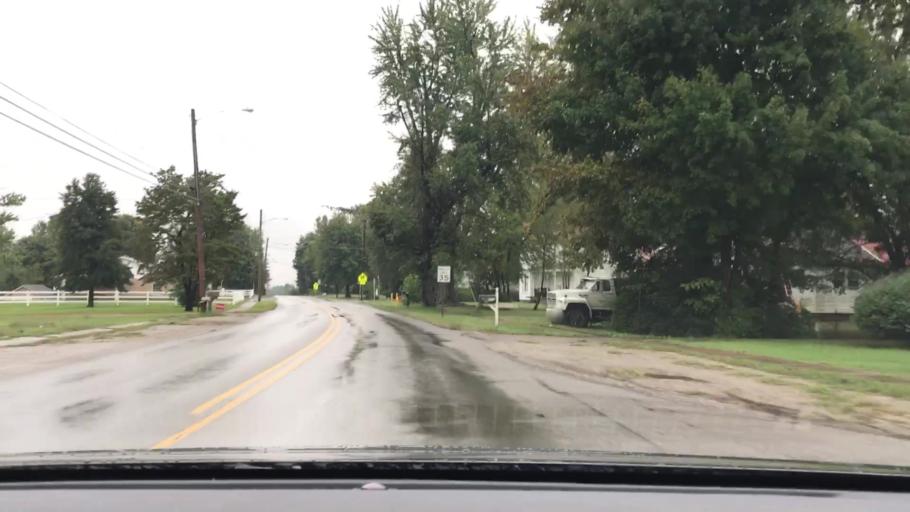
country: US
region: Kentucky
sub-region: McLean County
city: Calhoun
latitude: 37.4146
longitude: -87.2658
